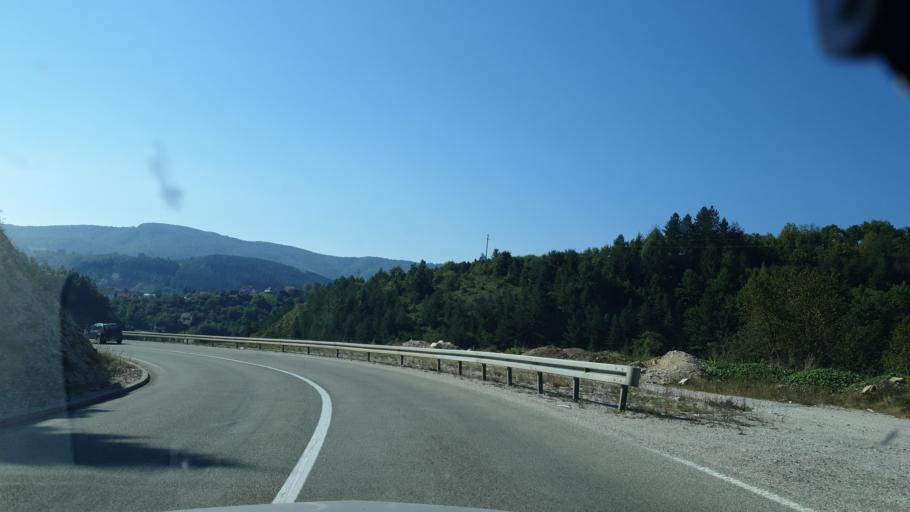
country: RS
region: Central Serbia
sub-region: Zlatiborski Okrug
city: Nova Varos
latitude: 43.5240
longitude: 19.8012
